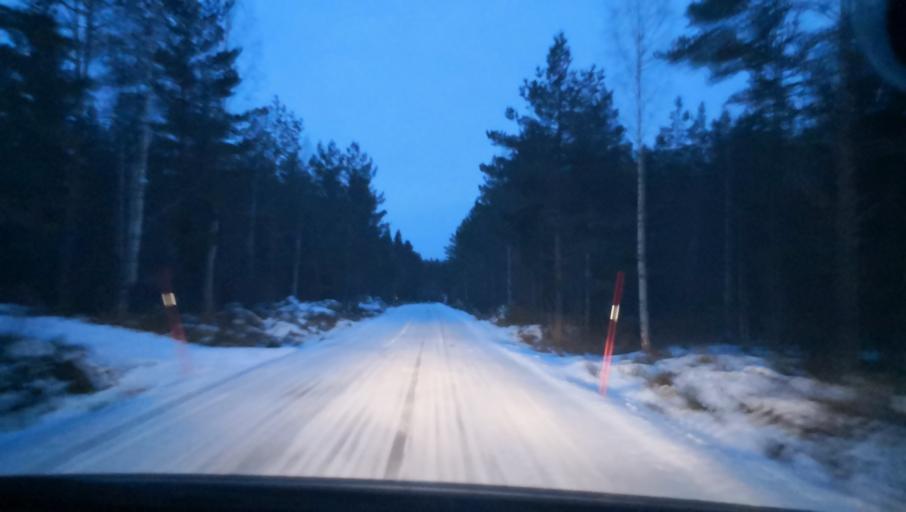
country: SE
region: Dalarna
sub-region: Avesta Kommun
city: Horndal
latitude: 60.2380
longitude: 16.6663
